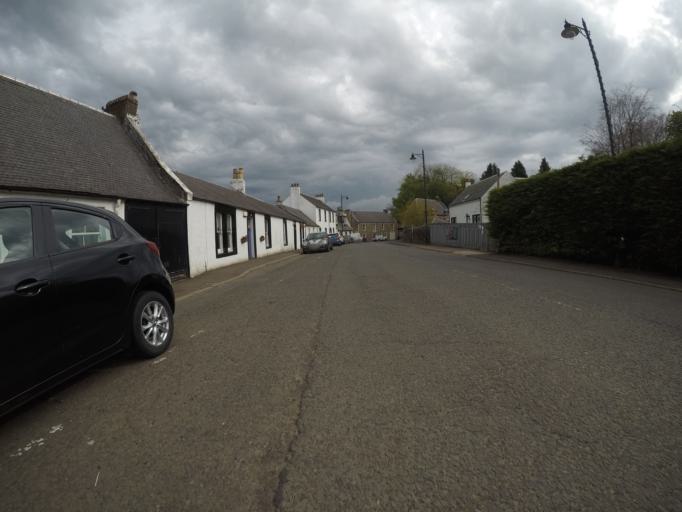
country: GB
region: Scotland
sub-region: East Ayrshire
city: Kilmarnock
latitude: 55.6549
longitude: -4.4456
